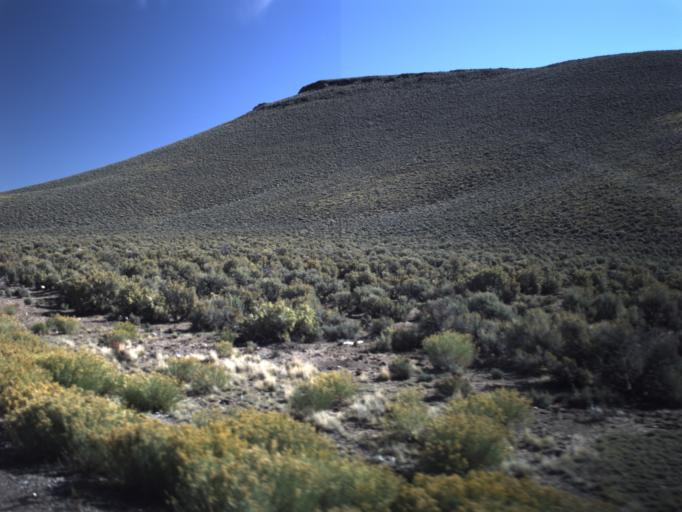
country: US
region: Utah
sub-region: Piute County
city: Junction
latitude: 38.2765
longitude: -111.9841
